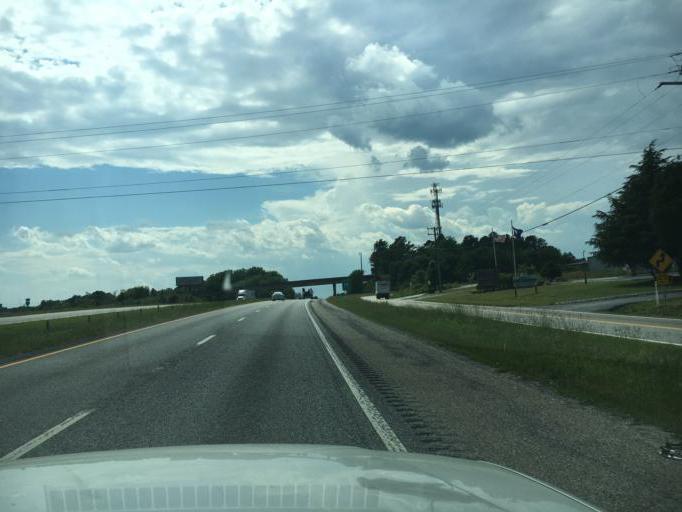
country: US
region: South Carolina
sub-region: Spartanburg County
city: Fairforest
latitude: 34.9650
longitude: -82.0186
